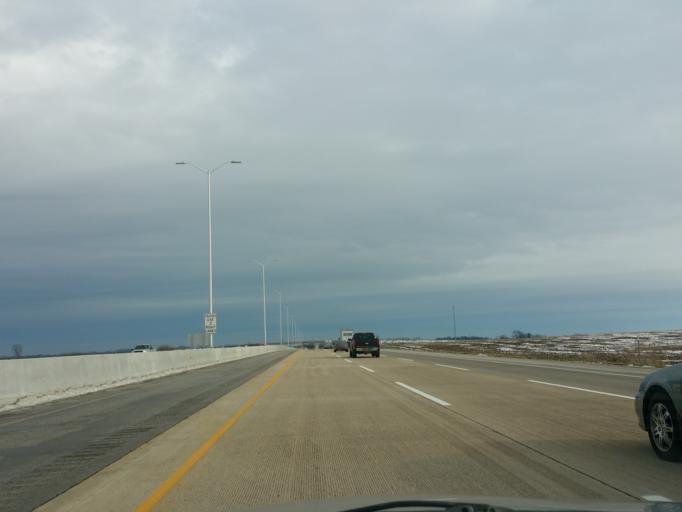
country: US
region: Illinois
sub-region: Boone County
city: Belvidere
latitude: 42.2335
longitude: -88.7969
